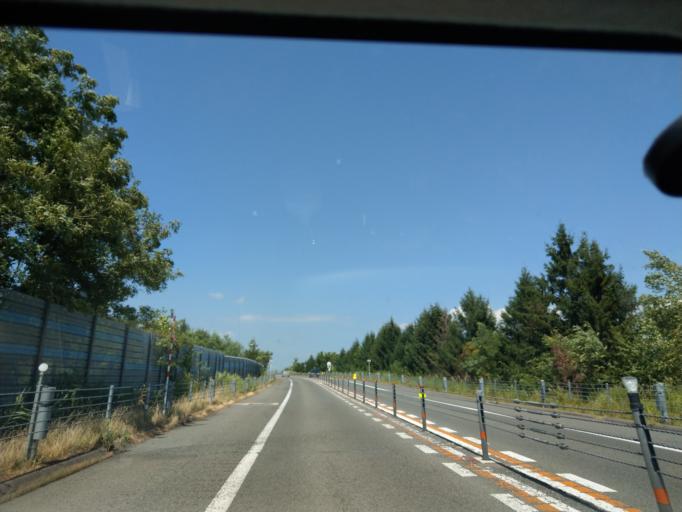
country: JP
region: Akita
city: Yokotemachi
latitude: 39.3503
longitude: 140.4971
